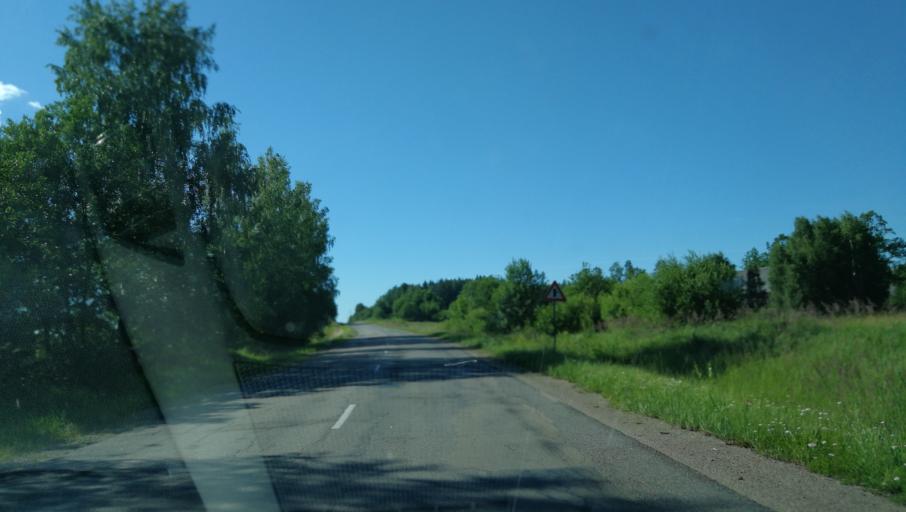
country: LV
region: Jaunpiebalga
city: Jaunpiebalga
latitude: 56.9789
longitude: 26.0366
